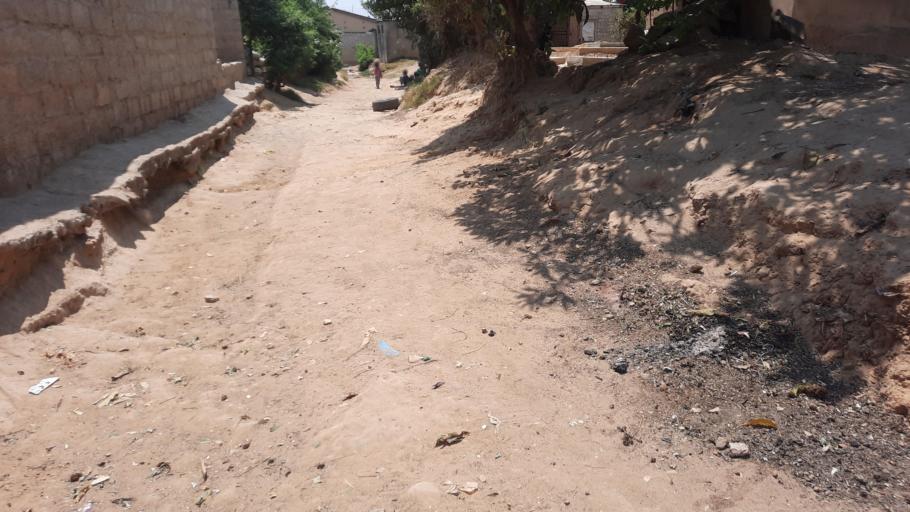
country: ZM
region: Lusaka
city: Lusaka
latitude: -15.3982
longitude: 28.3770
